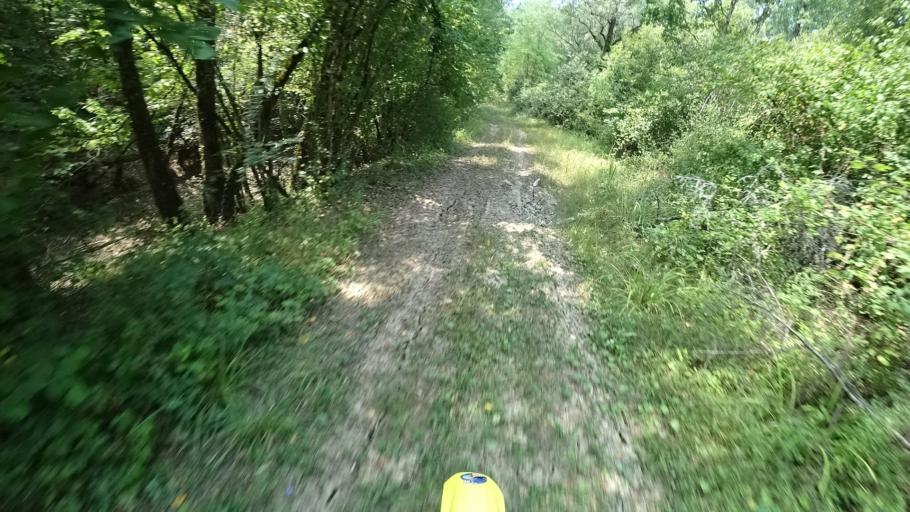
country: HR
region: Istarska
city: Karojba
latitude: 45.3468
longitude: 13.8501
